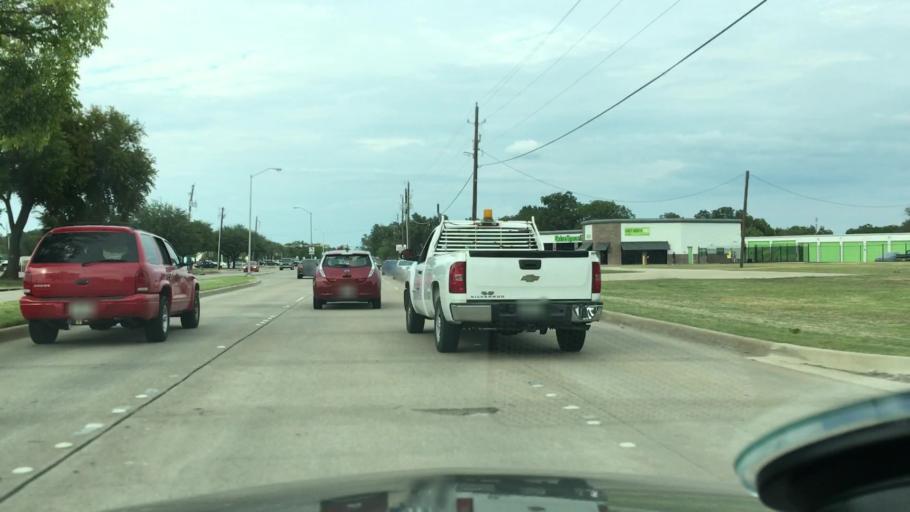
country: US
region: Texas
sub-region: Collin County
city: Plano
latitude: 33.0631
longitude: -96.6898
